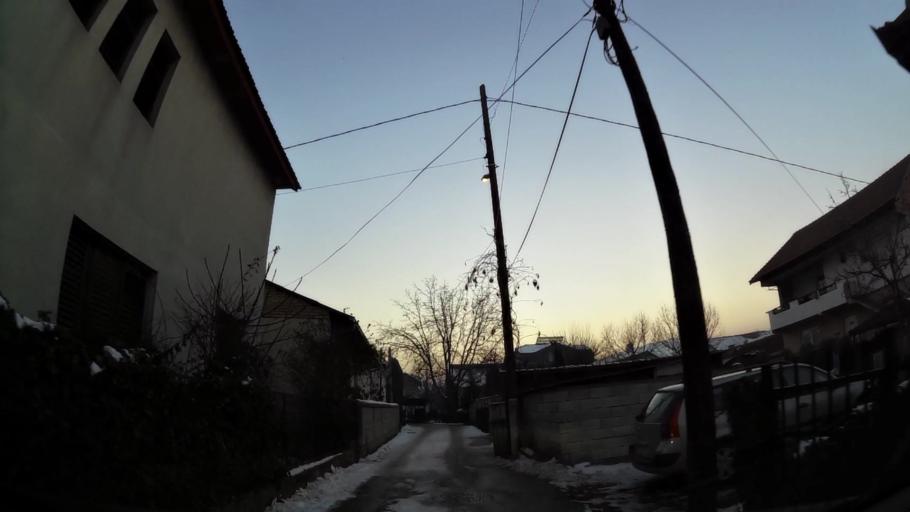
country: MK
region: Kisela Voda
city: Usje
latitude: 41.9808
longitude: 21.4853
